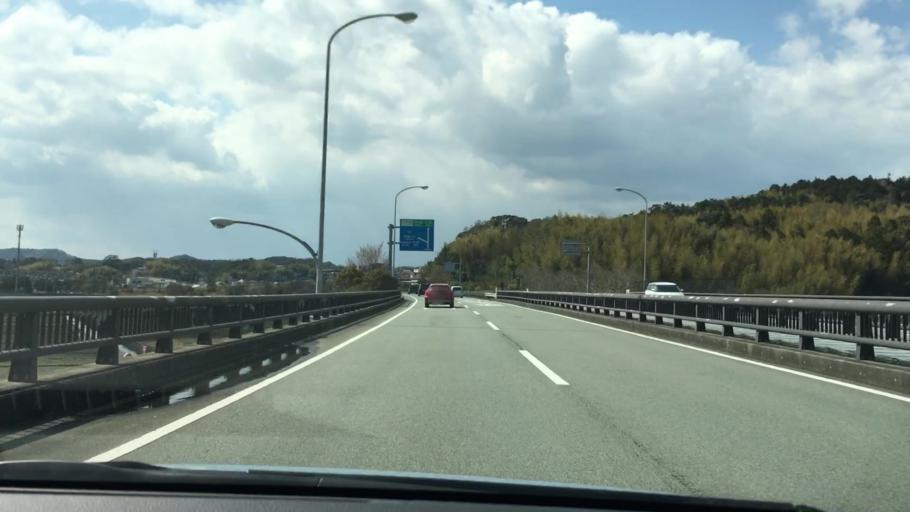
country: JP
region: Mie
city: Ise
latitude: 34.4797
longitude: 136.7387
